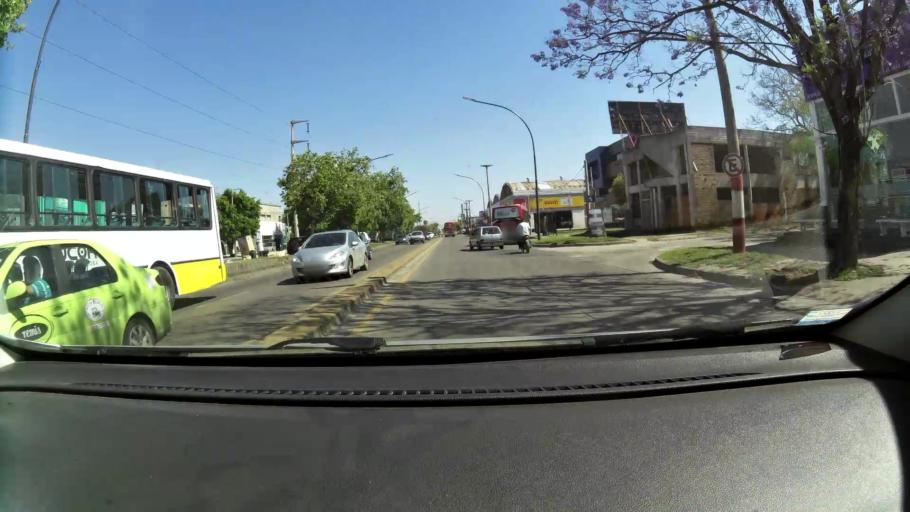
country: AR
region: Cordoba
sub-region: Departamento de Capital
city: Cordoba
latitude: -31.3787
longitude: -64.1760
